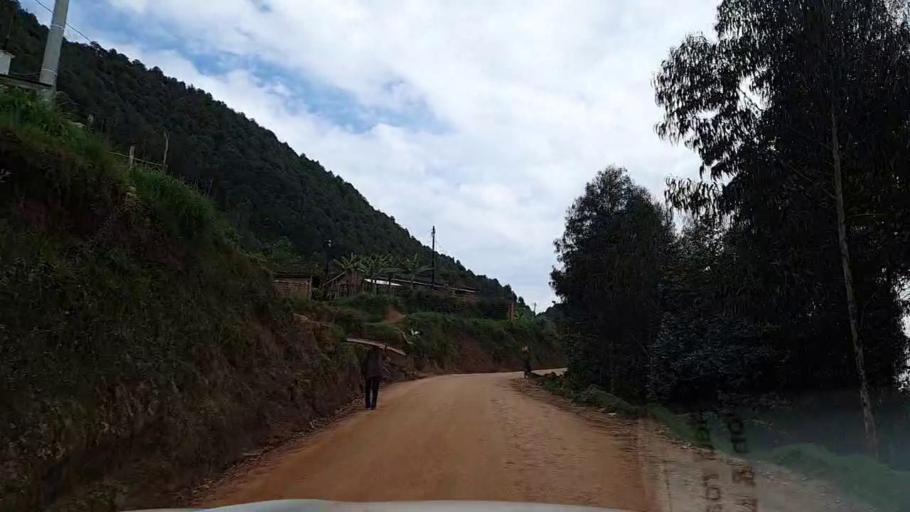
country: RW
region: Southern Province
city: Nzega
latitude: -2.3972
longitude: 29.4535
